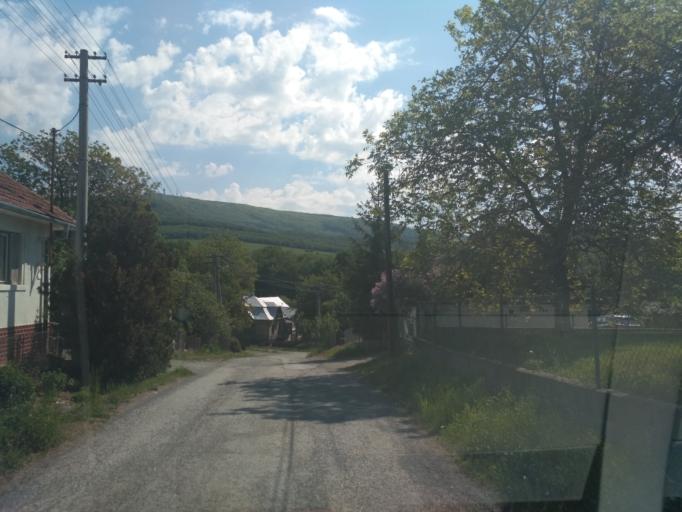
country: SK
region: Kosicky
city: Kosice
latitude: 48.8465
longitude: 21.4356
